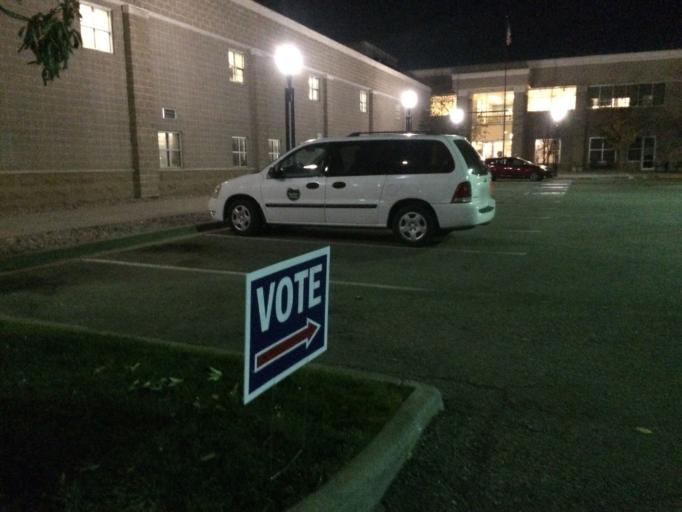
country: US
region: Colorado
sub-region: Boulder County
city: Boulder
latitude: 40.0177
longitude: -105.2490
